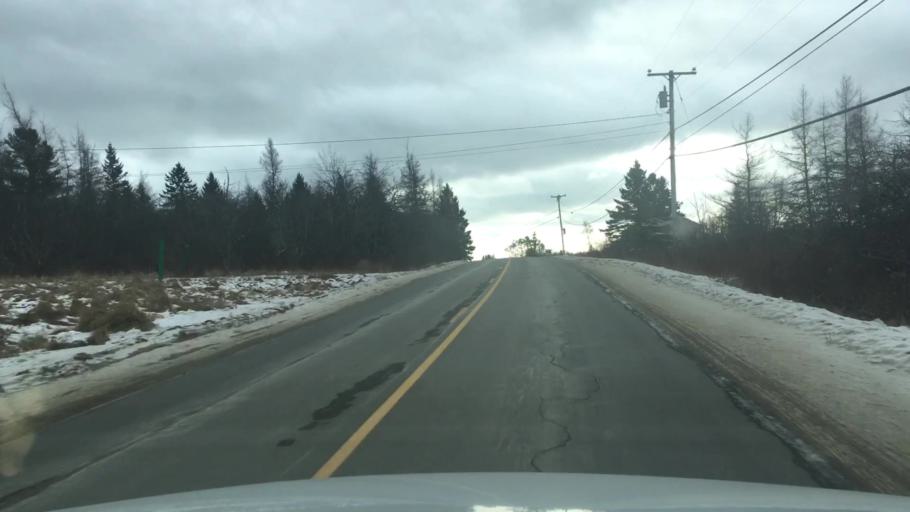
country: US
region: Maine
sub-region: Washington County
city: Machias
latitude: 44.6814
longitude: -67.4674
